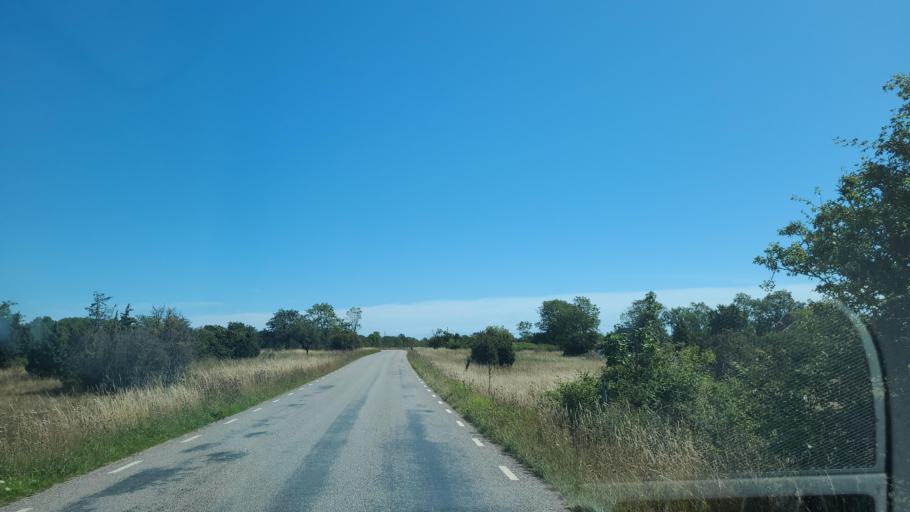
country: SE
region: Kalmar
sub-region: Borgholms Kommun
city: Borgholm
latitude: 56.7672
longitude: 16.5993
